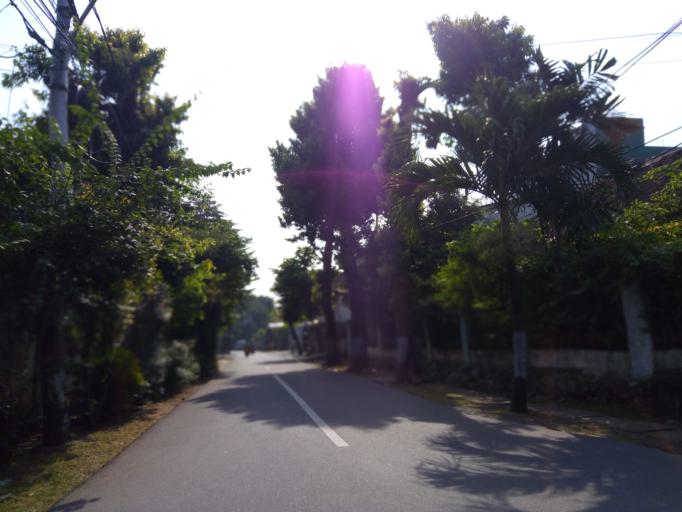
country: ID
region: Jakarta Raya
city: Jakarta
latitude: -6.2078
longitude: 106.8368
